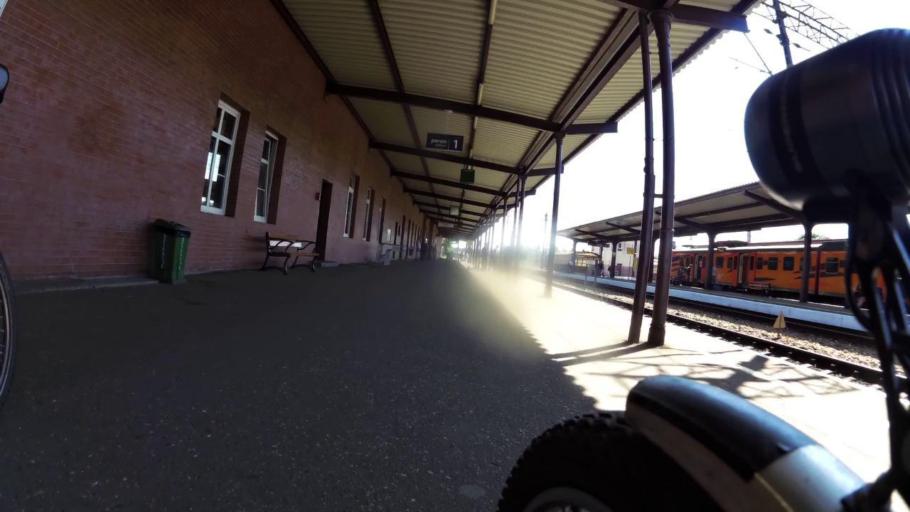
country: PL
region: West Pomeranian Voivodeship
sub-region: Powiat bialogardzki
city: Bialogard
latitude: 54.0100
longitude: 15.9778
